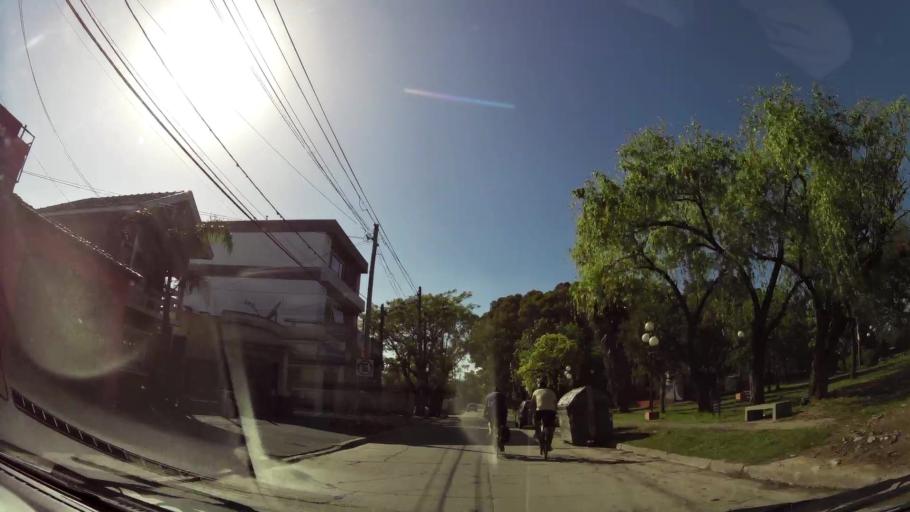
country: AR
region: Buenos Aires
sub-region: Partido de Quilmes
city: Quilmes
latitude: -34.7900
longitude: -58.1553
